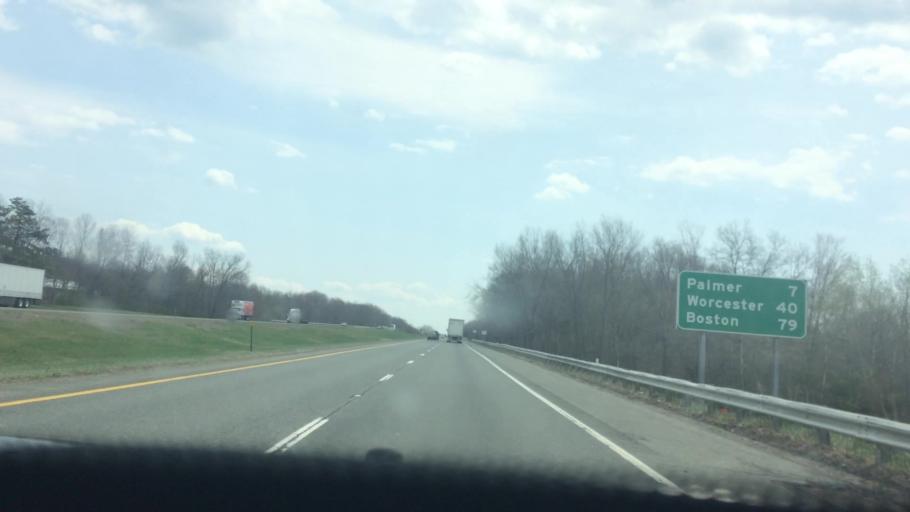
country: US
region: Massachusetts
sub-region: Hampden County
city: Ludlow
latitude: 42.1677
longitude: -72.4370
